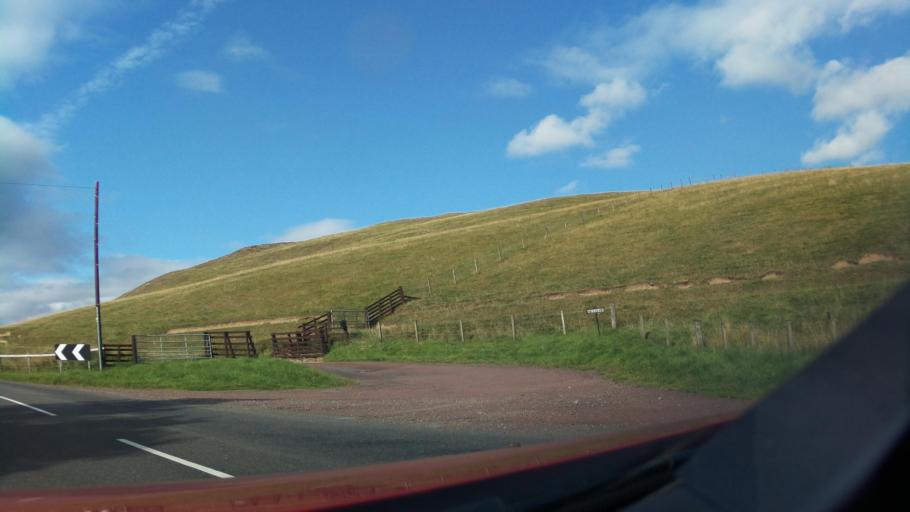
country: GB
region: Scotland
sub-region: South Lanarkshire
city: Biggar
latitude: 55.6453
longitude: -3.4280
